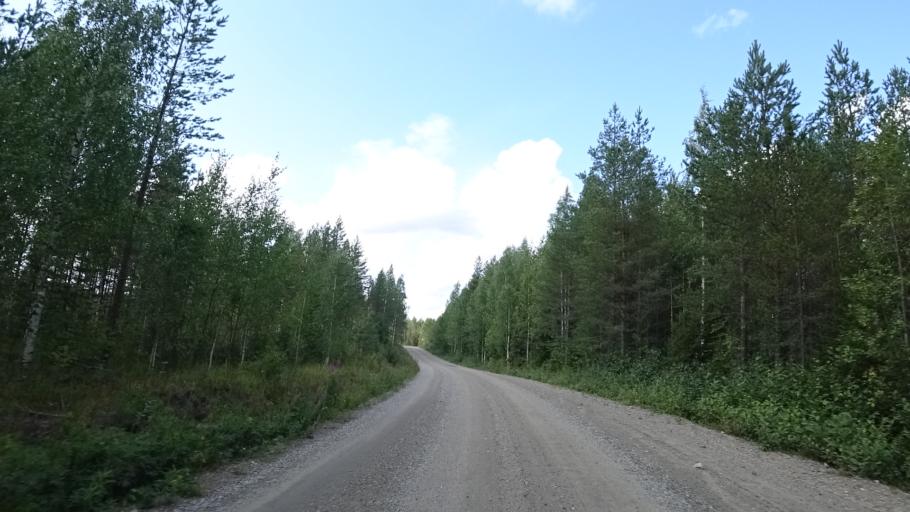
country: FI
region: North Karelia
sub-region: Joensuu
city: Ilomantsi
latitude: 62.9269
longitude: 31.3293
